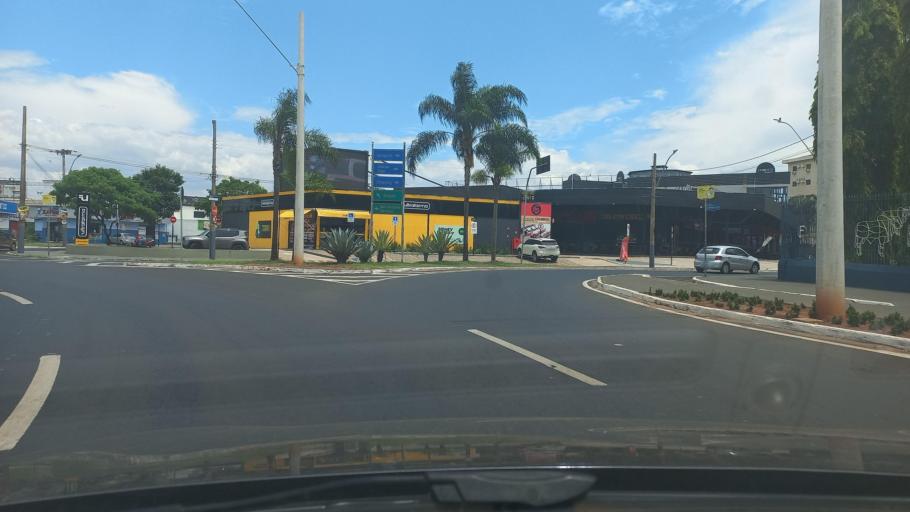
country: BR
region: Minas Gerais
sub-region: Uberaba
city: Uberaba
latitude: -19.7701
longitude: -47.9454
